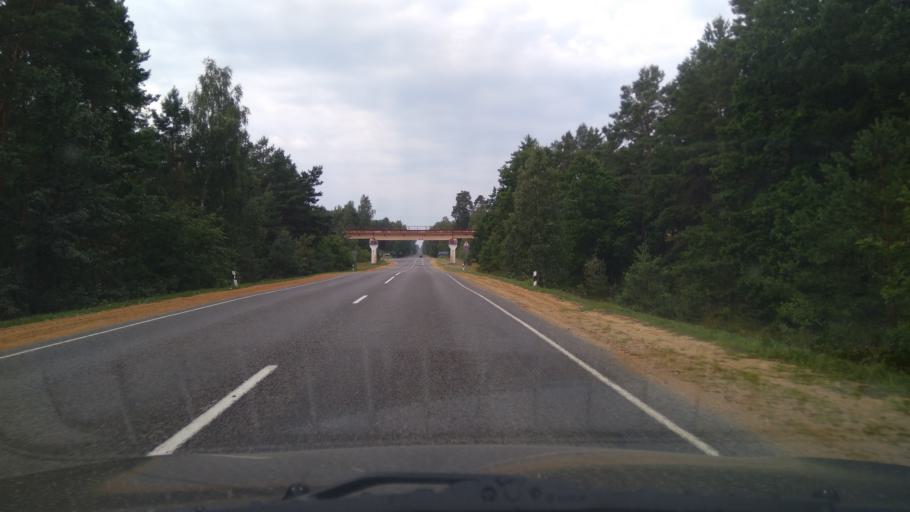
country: BY
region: Brest
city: Nyakhachava
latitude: 52.5898
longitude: 25.0961
